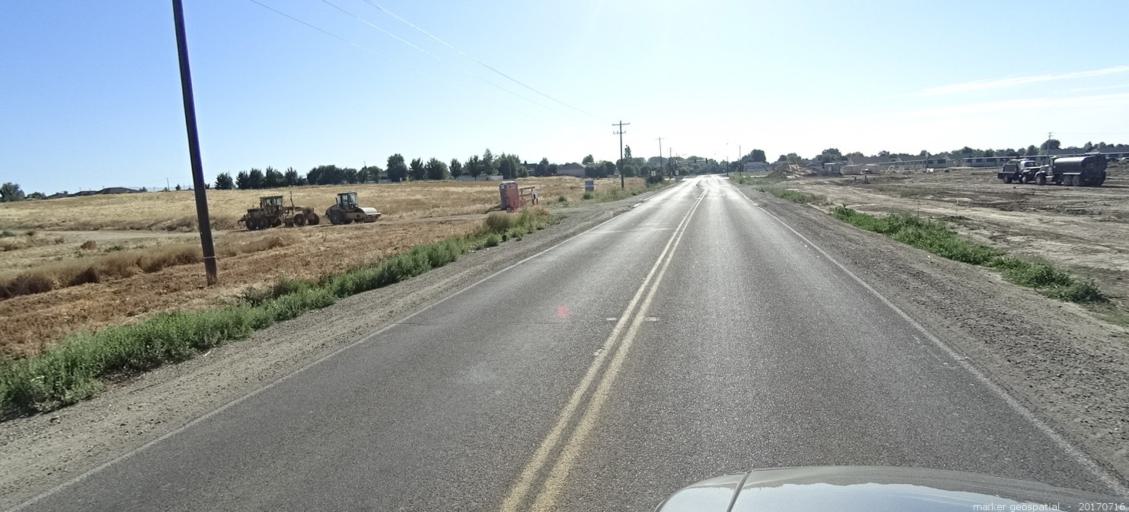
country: US
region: Idaho
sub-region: Ada County
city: Garden City
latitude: 43.5465
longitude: -116.2968
